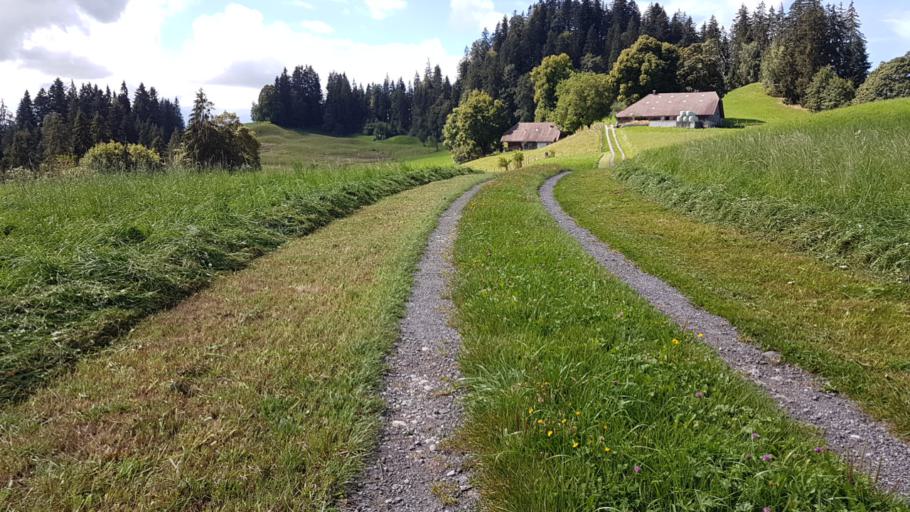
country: CH
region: Bern
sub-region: Bern-Mittelland District
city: Linden
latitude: 46.8433
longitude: 7.7168
